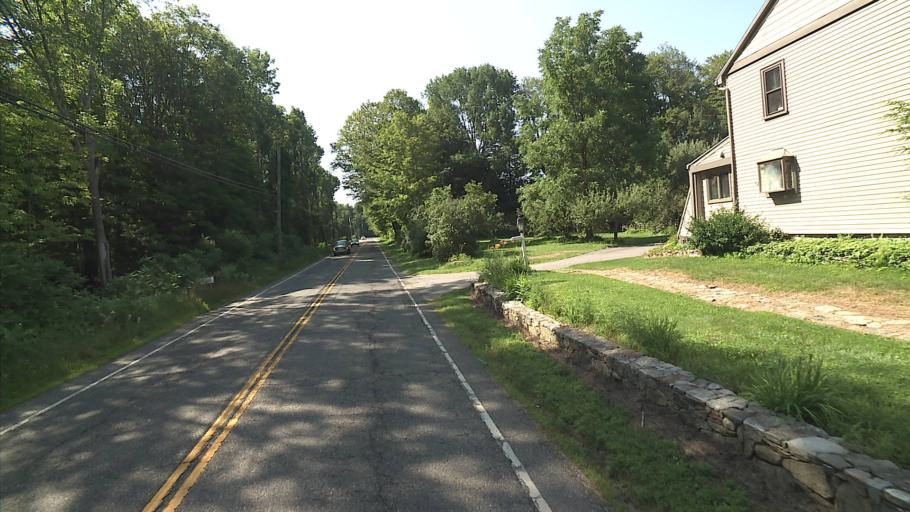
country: US
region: Connecticut
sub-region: Litchfield County
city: Winsted
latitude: 41.8882
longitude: -73.0658
